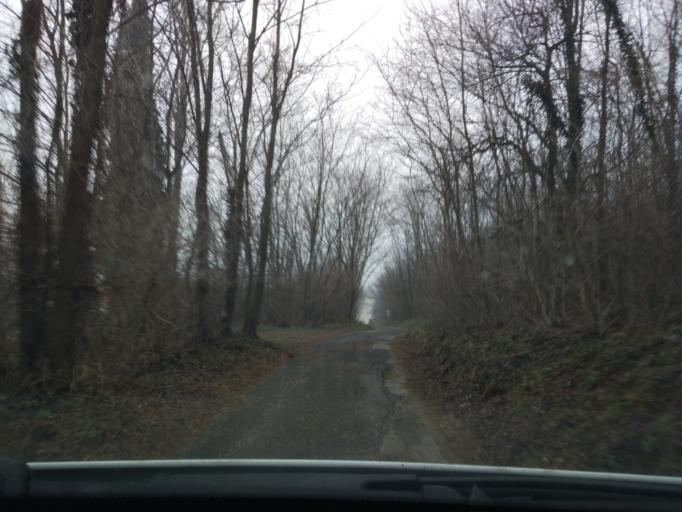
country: HU
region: Veszprem
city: Badacsonytomaj
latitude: 46.8121
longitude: 17.5014
